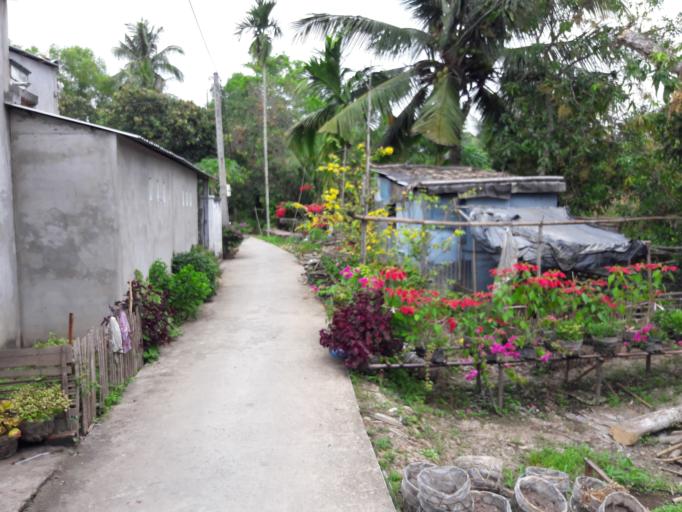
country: VN
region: Can Tho
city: Cai Rang
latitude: 10.0252
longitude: 105.7377
